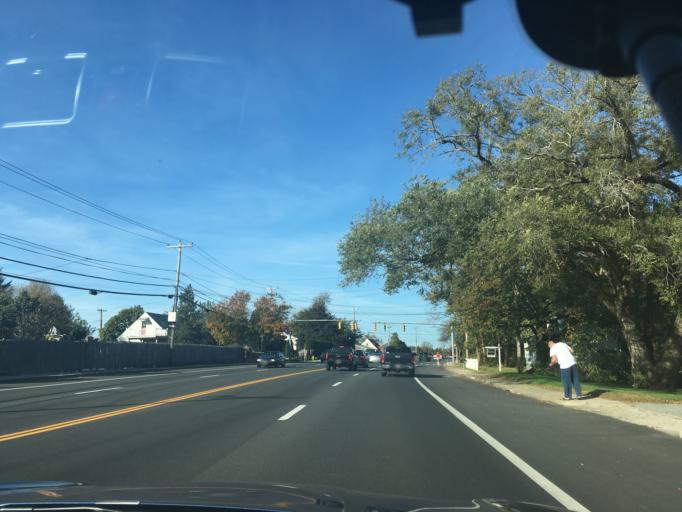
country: US
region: Rhode Island
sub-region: Washington County
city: Narragansett Pier
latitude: 41.4023
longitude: -71.4794
